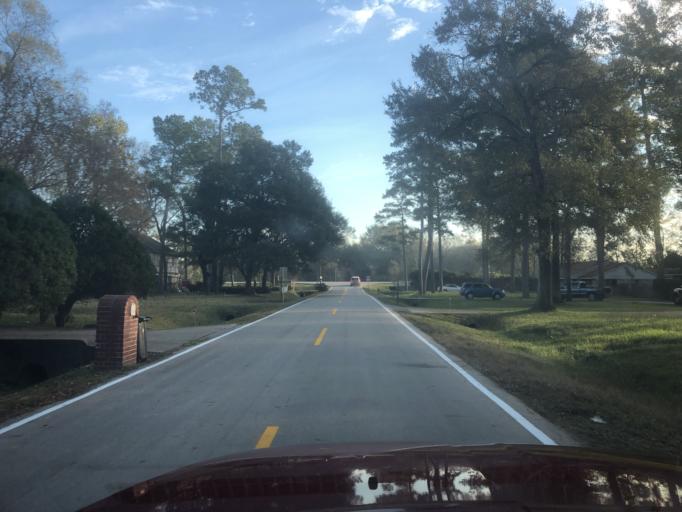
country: US
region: Texas
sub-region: Harris County
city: Spring
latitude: 30.0197
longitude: -95.4744
